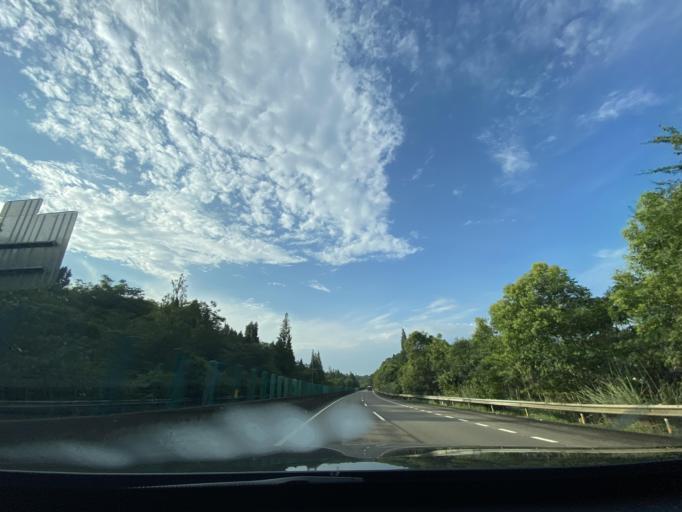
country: CN
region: Sichuan
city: Jiancheng
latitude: 30.3069
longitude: 104.5780
